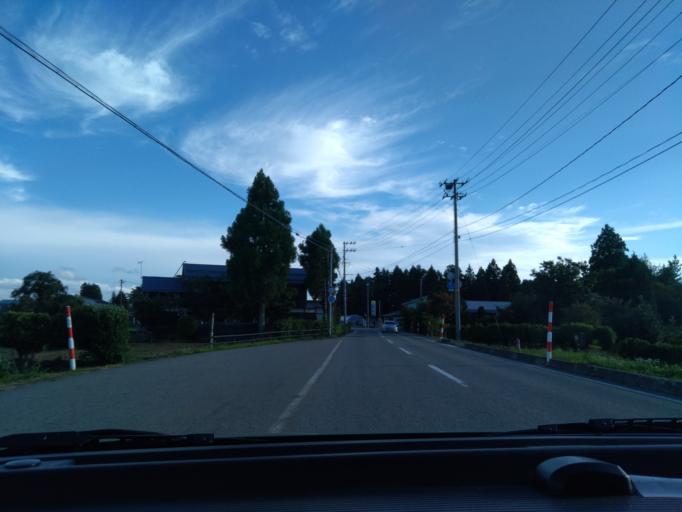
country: JP
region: Akita
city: Omagari
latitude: 39.4221
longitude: 140.4865
